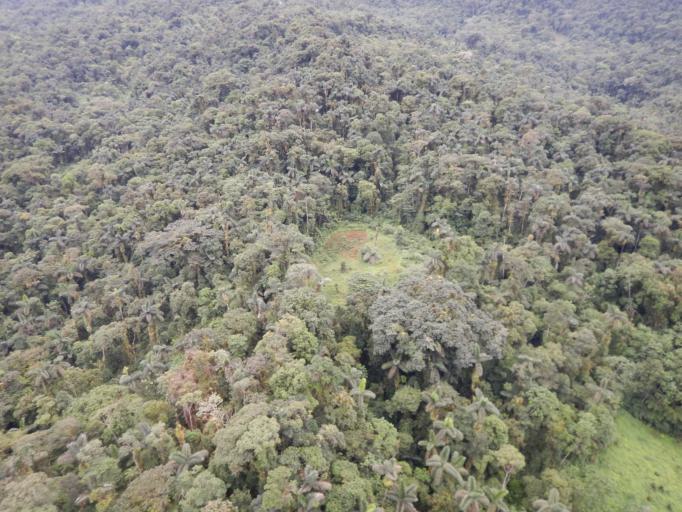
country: BO
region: Cochabamba
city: Totora
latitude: -17.3750
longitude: -65.2437
